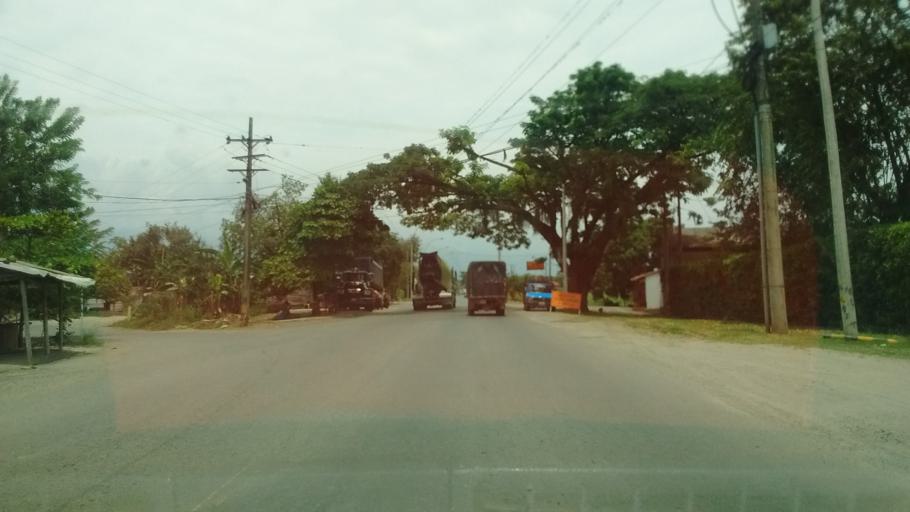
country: CO
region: Valle del Cauca
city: Jamundi
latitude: 3.3168
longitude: -76.4914
